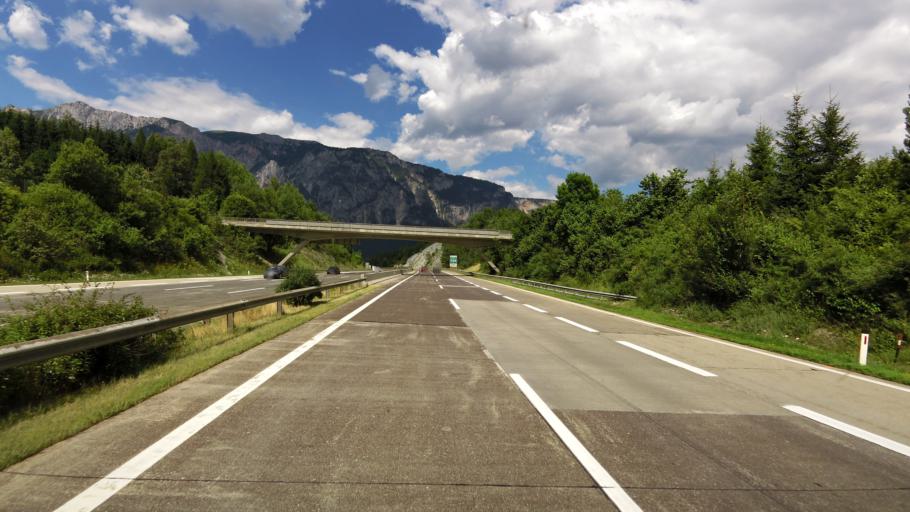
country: AT
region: Carinthia
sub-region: Politischer Bezirk Villach Land
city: Hohenthurn
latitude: 46.5513
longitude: 13.6825
